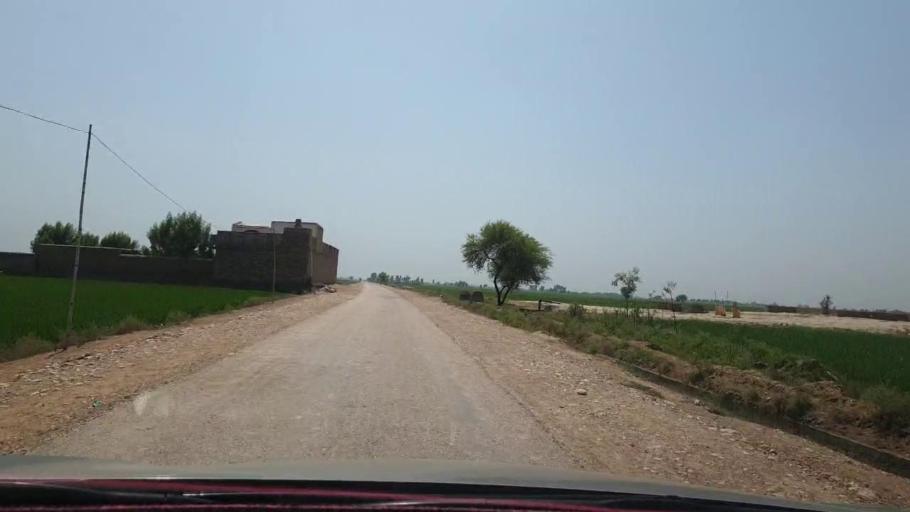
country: PK
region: Sindh
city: Warah
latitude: 27.5690
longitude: 67.8038
